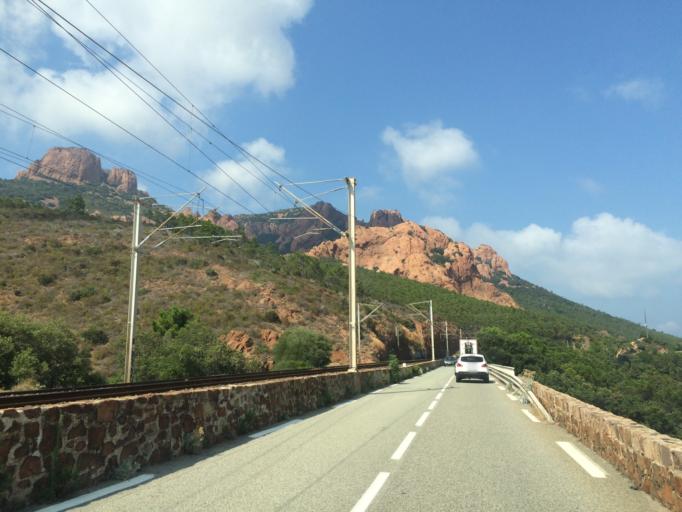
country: FR
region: Provence-Alpes-Cote d'Azur
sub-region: Departement des Alpes-Maritimes
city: Theoule-sur-Mer
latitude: 43.4418
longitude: 6.8981
